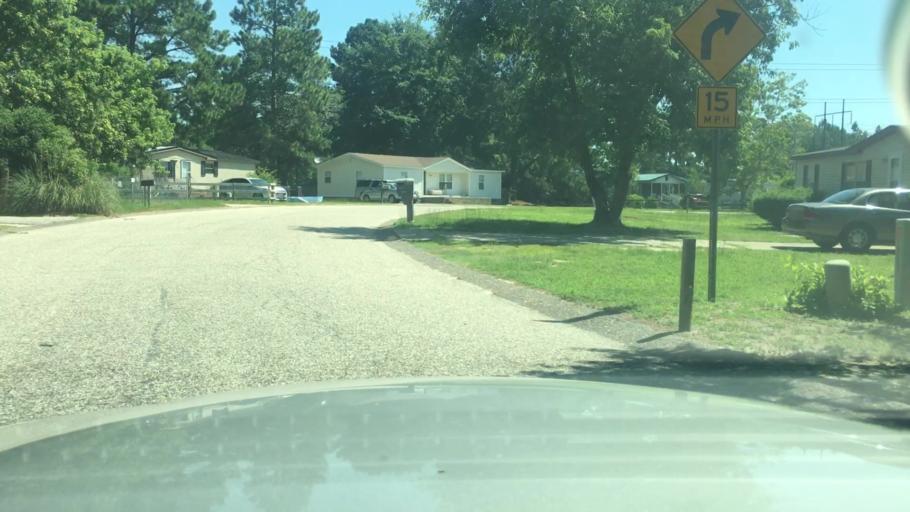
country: US
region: North Carolina
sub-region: Cumberland County
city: Hope Mills
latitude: 34.9742
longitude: -78.9090
